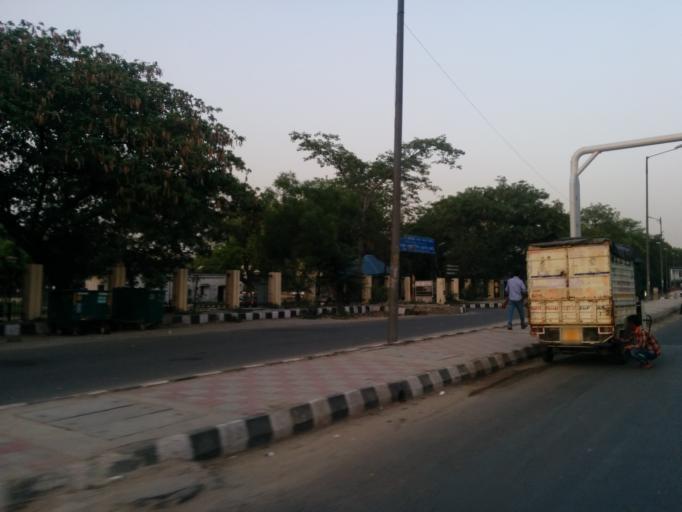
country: IN
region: NCT
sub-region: New Delhi
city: New Delhi
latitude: 28.5699
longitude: 77.2024
